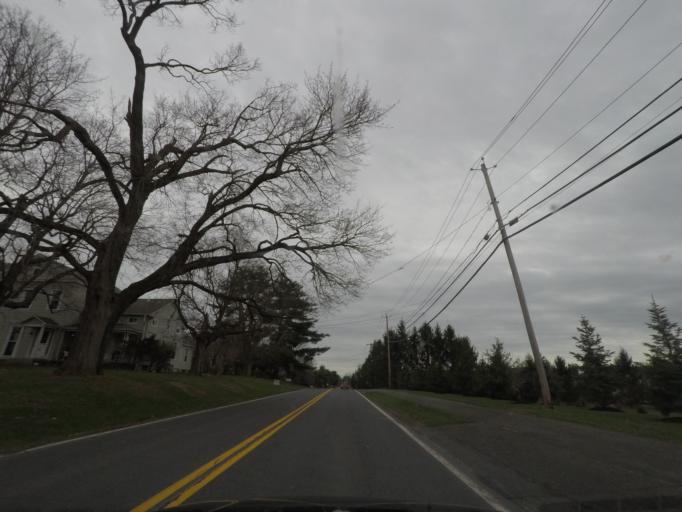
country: US
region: New York
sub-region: Albany County
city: Delmar
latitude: 42.5984
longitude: -73.8118
